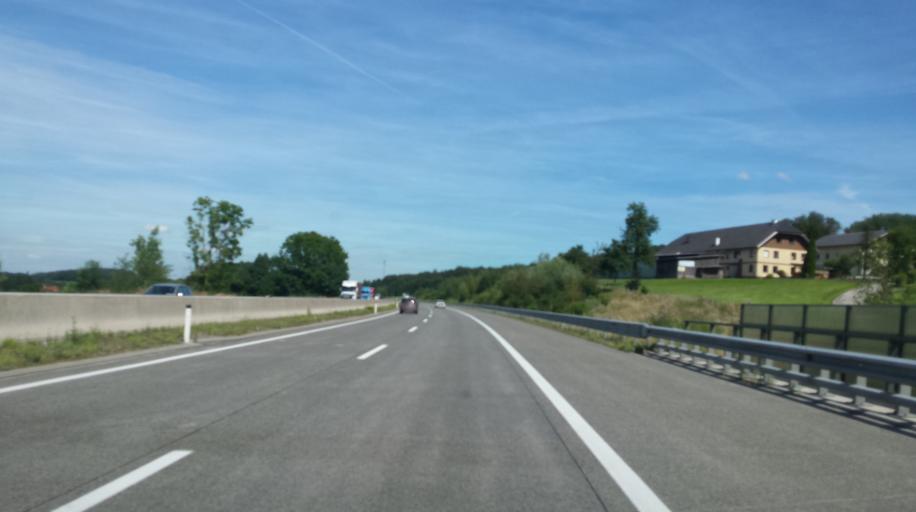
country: AT
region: Upper Austria
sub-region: Politischer Bezirk Vocklabruck
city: Aurach am Hongar
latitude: 47.9482
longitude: 13.6822
